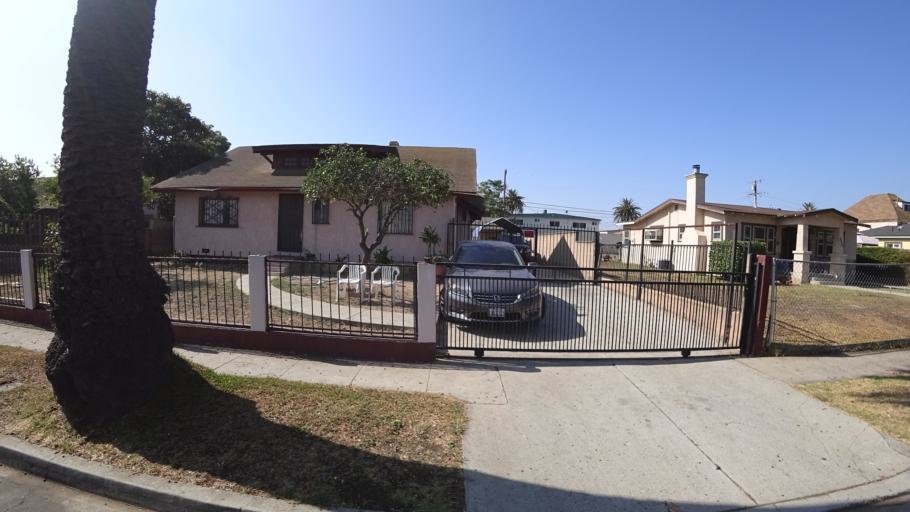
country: US
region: California
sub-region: Los Angeles County
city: Westmont
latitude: 33.9441
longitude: -118.3019
